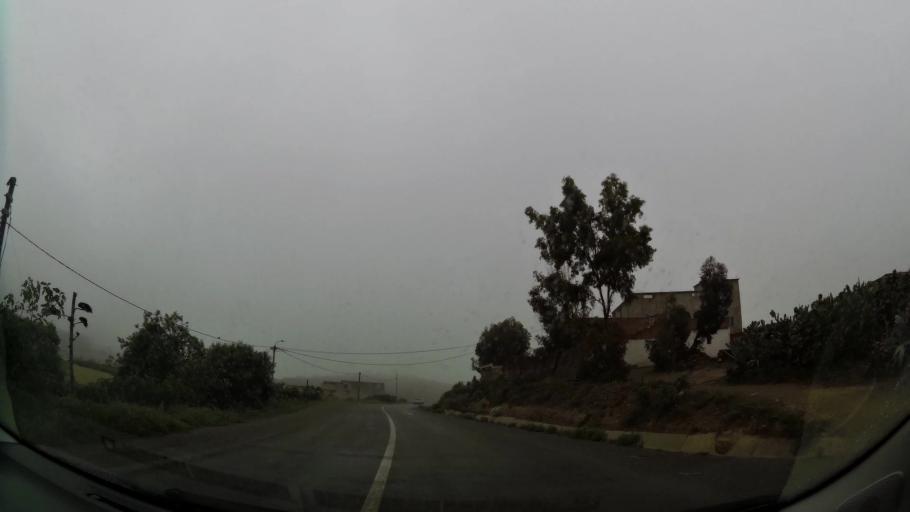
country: MA
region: Oriental
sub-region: Nador
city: Boudinar
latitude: 35.1266
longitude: -3.5789
